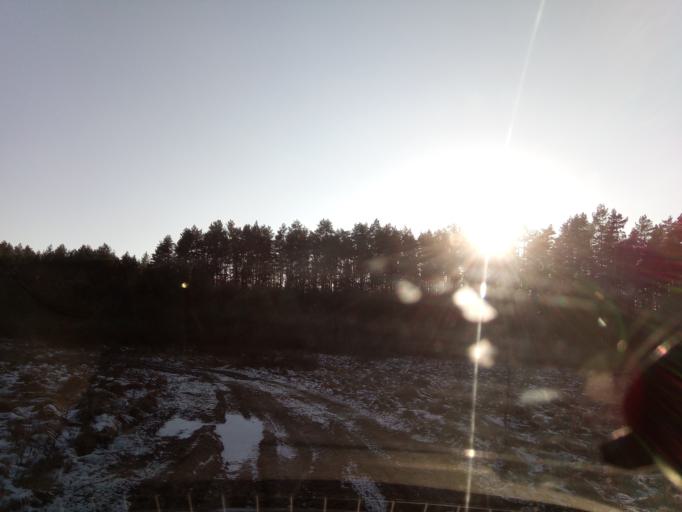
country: LT
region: Alytaus apskritis
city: Druskininkai
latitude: 53.9480
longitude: 23.8763
